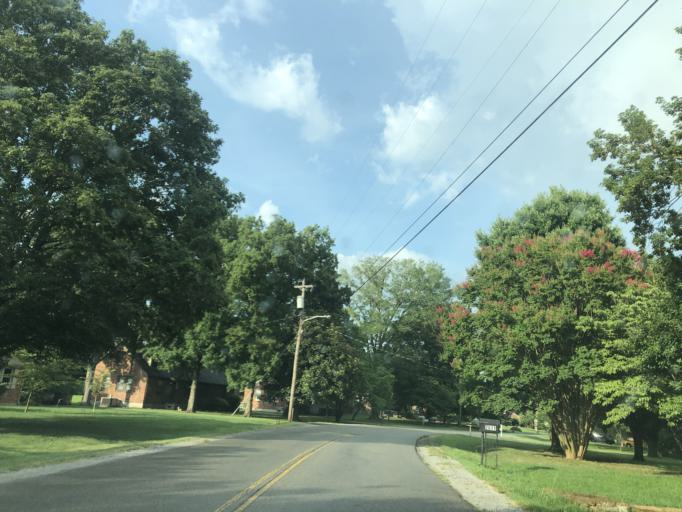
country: US
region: Tennessee
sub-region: Davidson County
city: Lakewood
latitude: 36.1551
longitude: -86.6743
